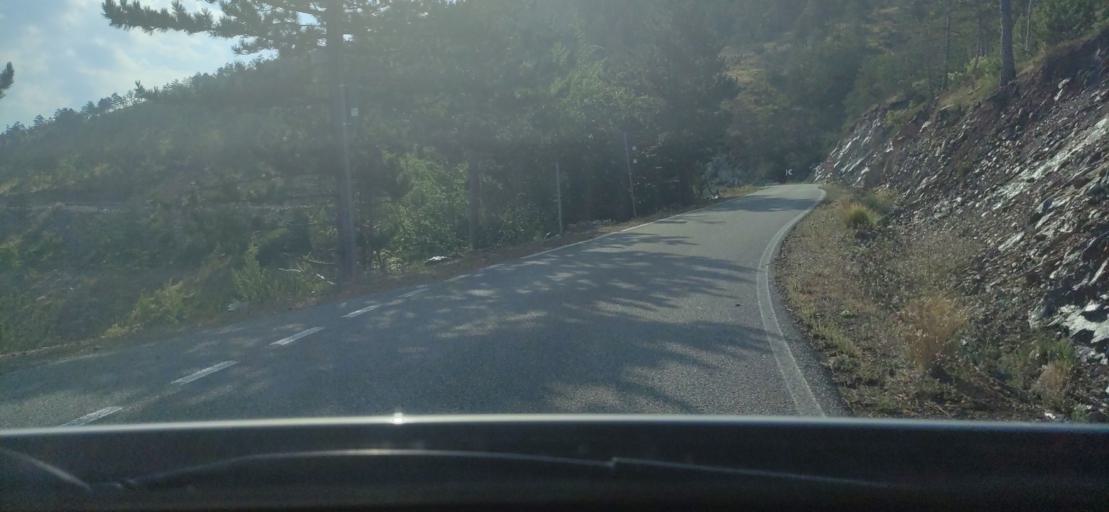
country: AL
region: Shkoder
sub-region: Rrethi i Pukes
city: Iballe
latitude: 42.1711
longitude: 20.0192
